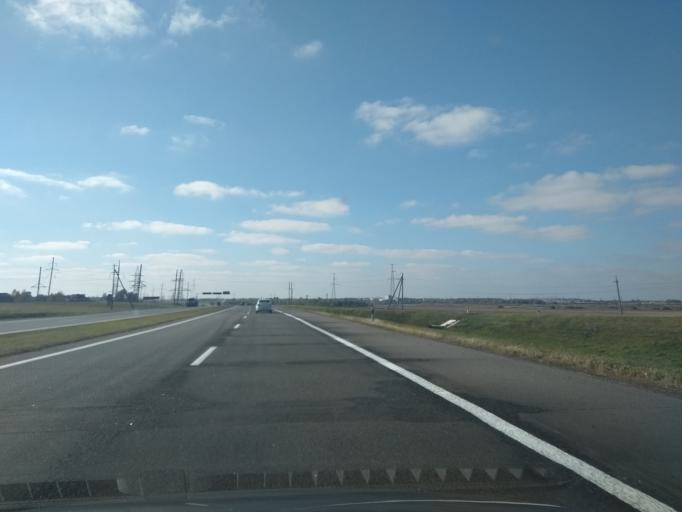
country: BY
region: Brest
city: Baranovichi
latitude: 53.1796
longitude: 26.0248
